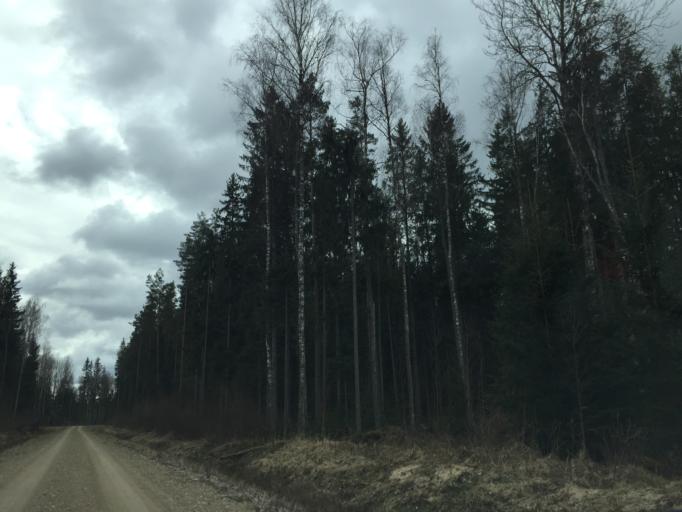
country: LV
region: Akniste
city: Akniste
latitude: 56.0786
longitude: 25.7618
